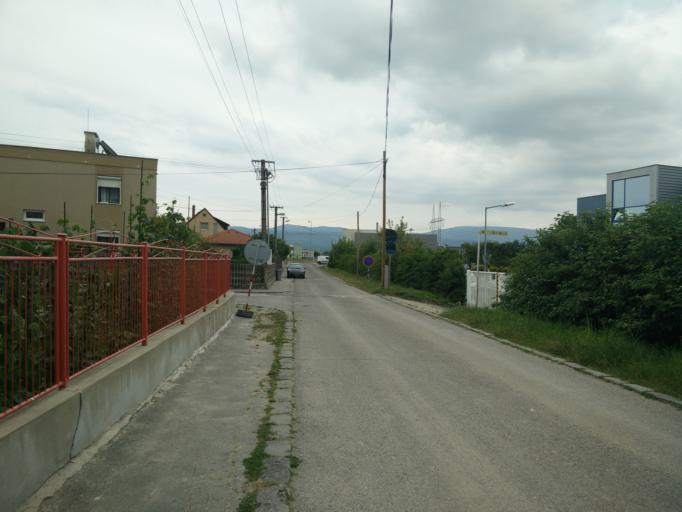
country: SK
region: Nitriansky
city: Bojnice
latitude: 48.7763
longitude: 18.5869
